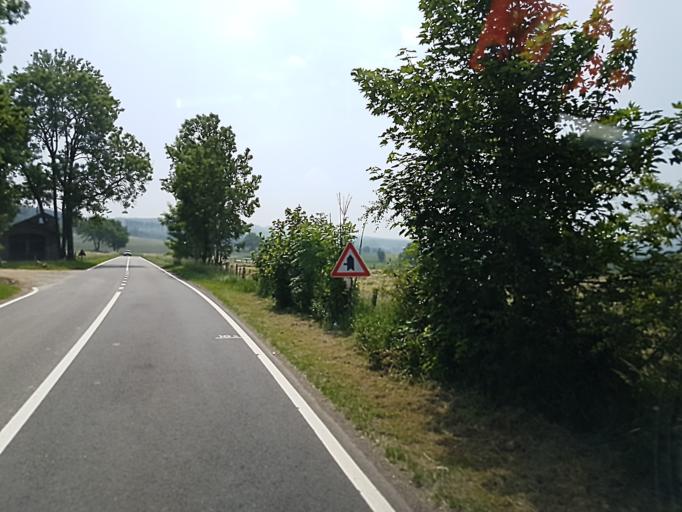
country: BE
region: Wallonia
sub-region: Province du Luxembourg
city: Manhay
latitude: 50.3148
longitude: 5.7264
